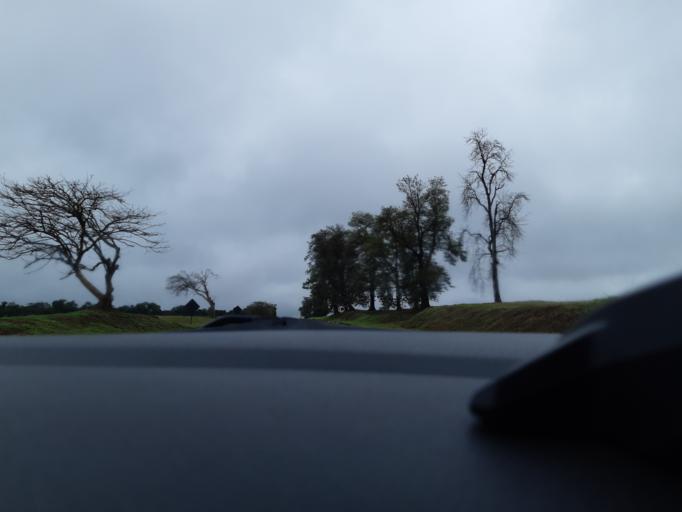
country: BR
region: Sao Paulo
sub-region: Ourinhos
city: Ourinhos
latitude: -23.0013
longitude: -49.9464
